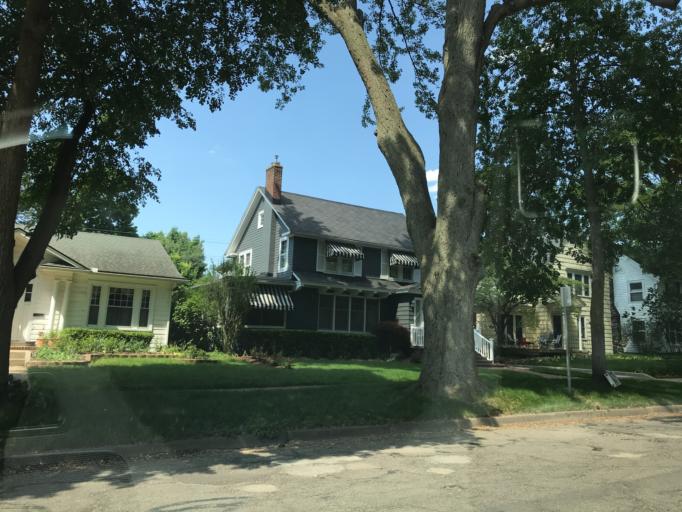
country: US
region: Michigan
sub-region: Washtenaw County
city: Ann Arbor
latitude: 42.2644
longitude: -83.7277
